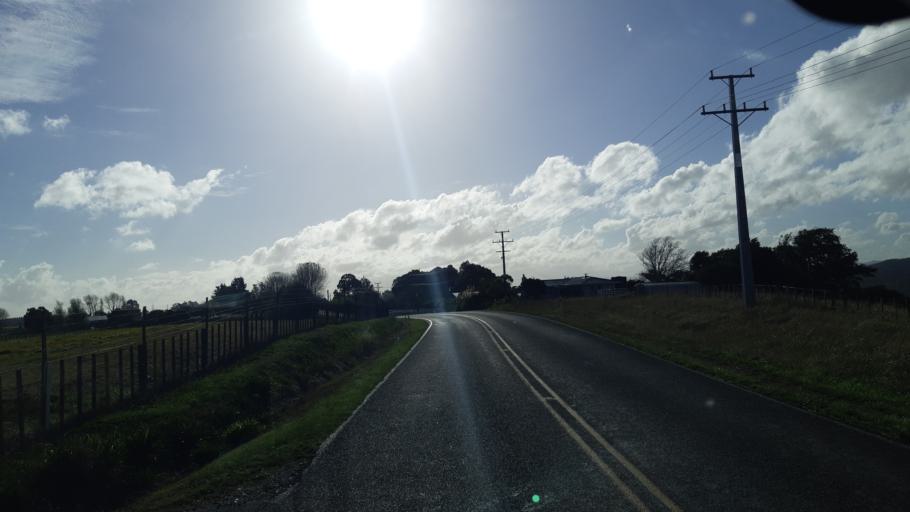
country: NZ
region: Manawatu-Wanganui
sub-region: Wanganui District
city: Wanganui
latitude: -39.9443
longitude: 175.1377
